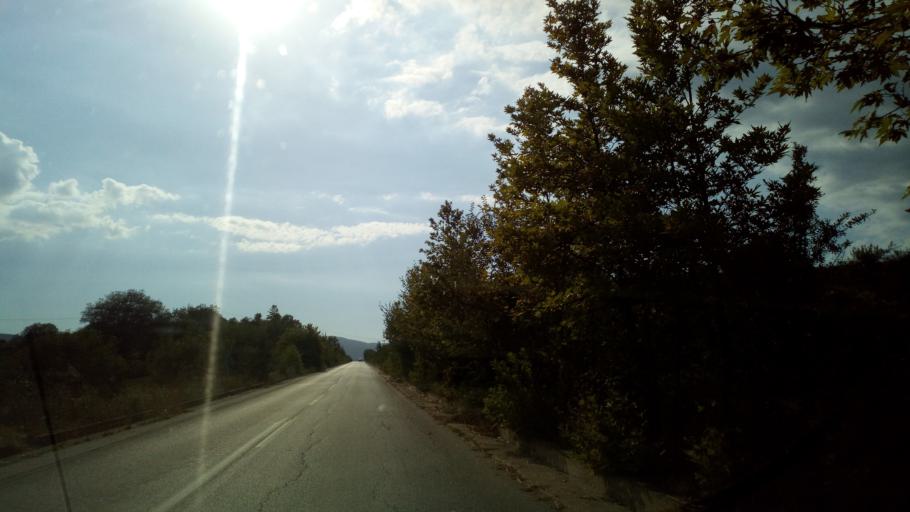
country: GR
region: Central Macedonia
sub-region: Nomos Thessalonikis
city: Gerakarou
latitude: 40.5899
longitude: 23.2522
